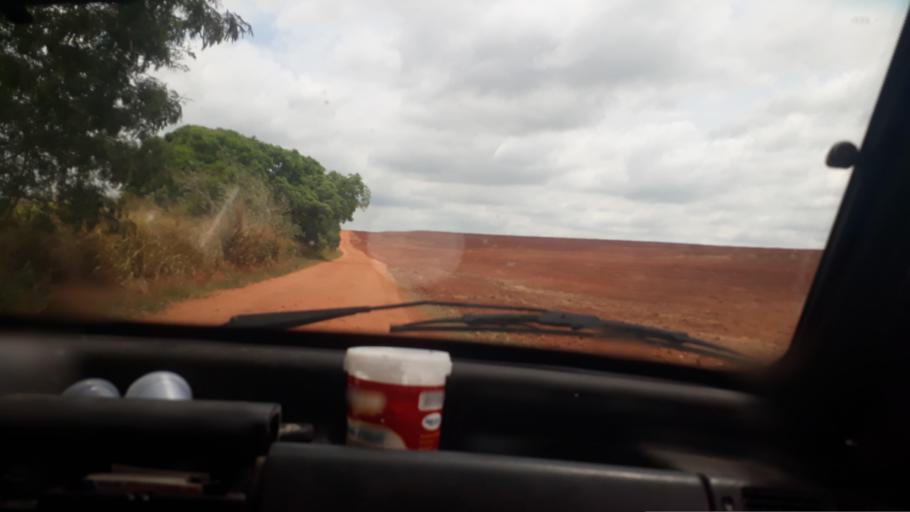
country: BR
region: Sao Paulo
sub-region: Regente Feijo
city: Regente Feijo
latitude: -22.2568
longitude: -51.3007
